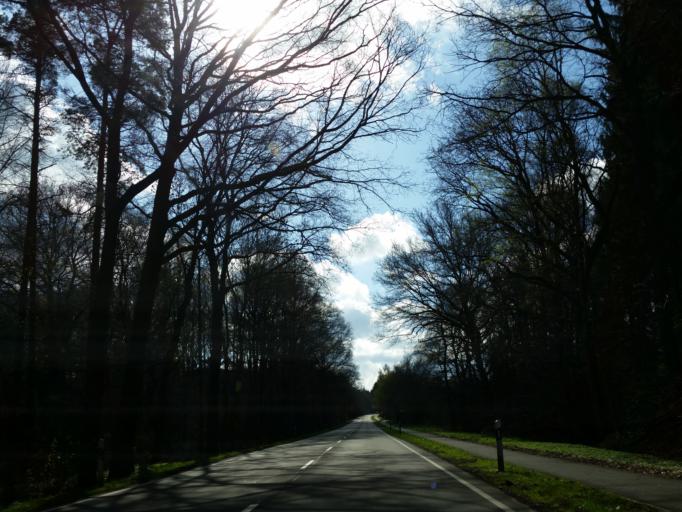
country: DE
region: Lower Saxony
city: Botersen
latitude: 53.1511
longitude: 9.3317
